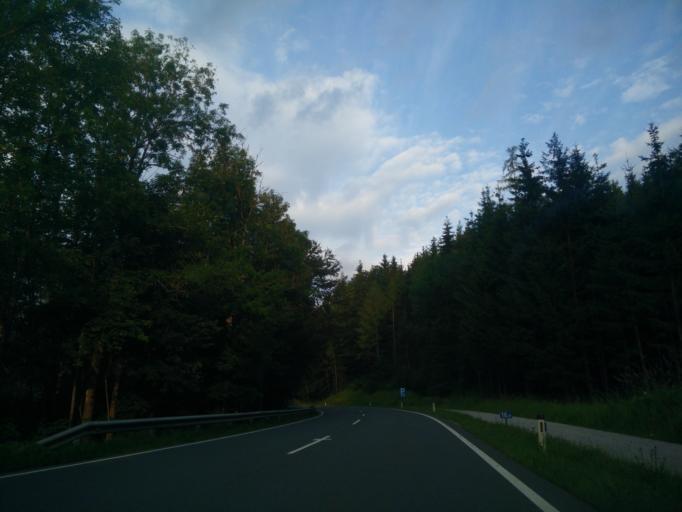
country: AT
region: Salzburg
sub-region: Politischer Bezirk Salzburg-Umgebung
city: Thalgau
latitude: 47.8035
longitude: 13.2550
